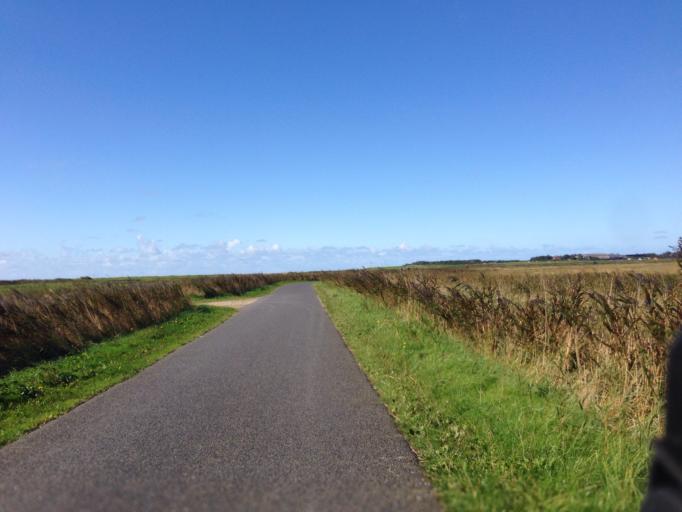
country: DE
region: Schleswig-Holstein
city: Witsum
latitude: 54.6965
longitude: 8.4301
